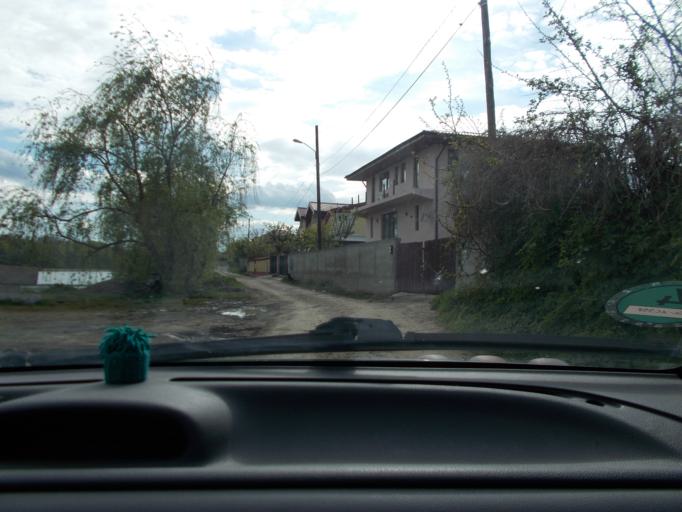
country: RO
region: Ilfov
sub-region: Comuna Branesti
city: Branesti
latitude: 44.4522
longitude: 26.3306
